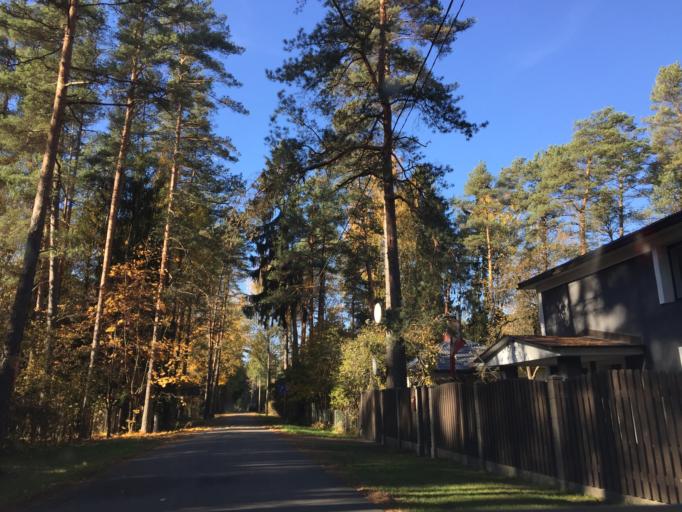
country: LV
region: Incukalns
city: Incukalns
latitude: 57.1009
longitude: 24.6750
